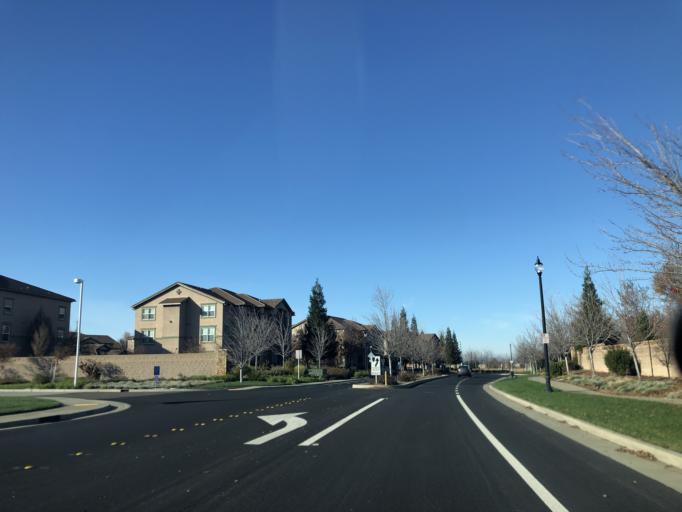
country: US
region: California
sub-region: Sacramento County
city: Antelope
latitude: 38.7894
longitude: -121.3713
